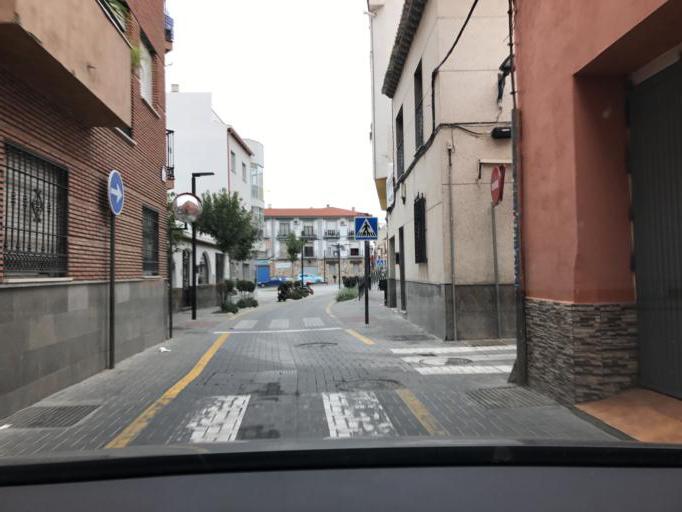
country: ES
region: Andalusia
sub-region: Provincia de Granada
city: Maracena
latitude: 37.2053
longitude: -3.6361
